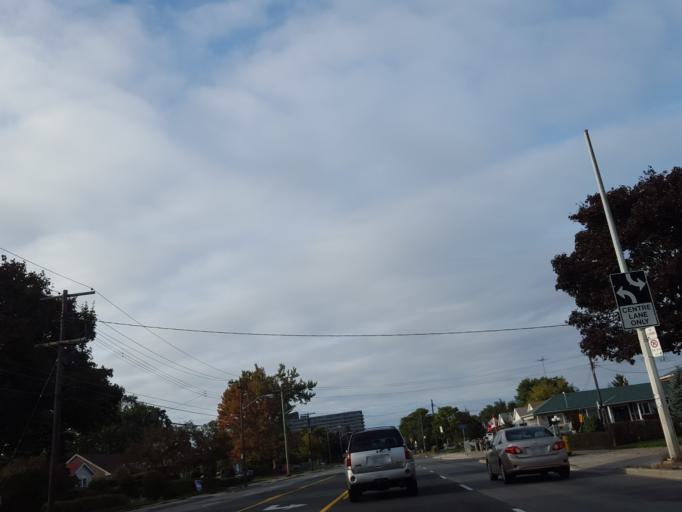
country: CA
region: Ontario
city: Scarborough
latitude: 43.7401
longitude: -79.2926
